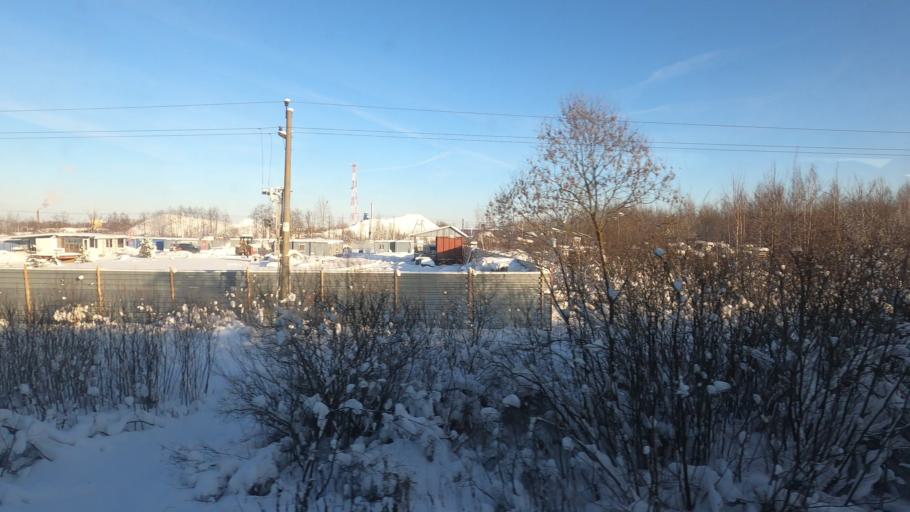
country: RU
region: Moskovskaya
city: Taldom
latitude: 56.7130
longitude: 37.5393
